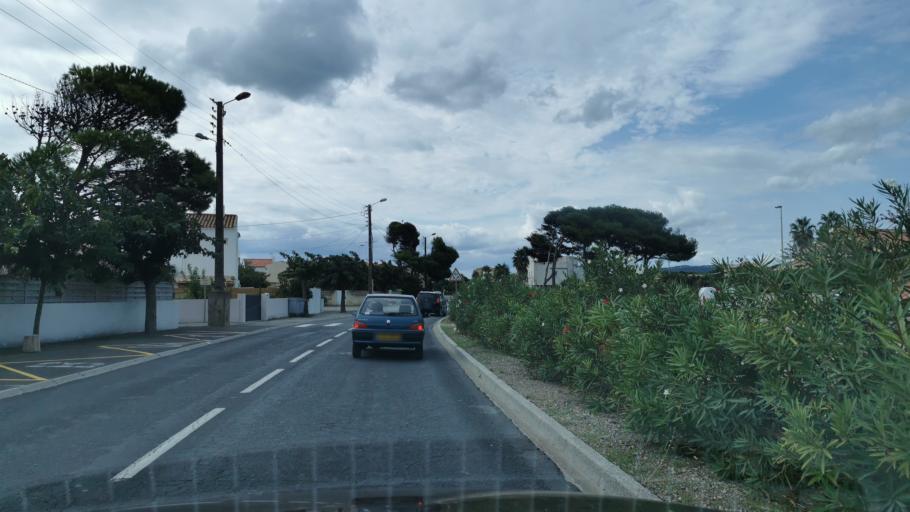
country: FR
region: Languedoc-Roussillon
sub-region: Departement de l'Aude
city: Fleury
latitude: 43.1637
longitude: 3.1716
